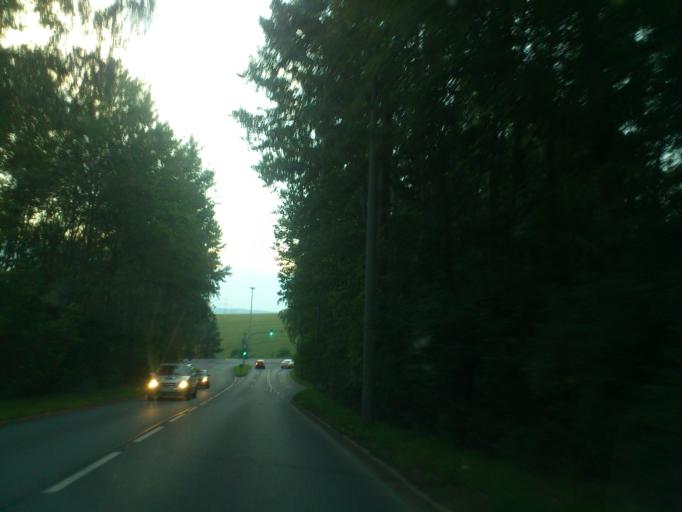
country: DE
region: Saxony
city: Neukirchen
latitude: 50.7852
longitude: 12.8747
